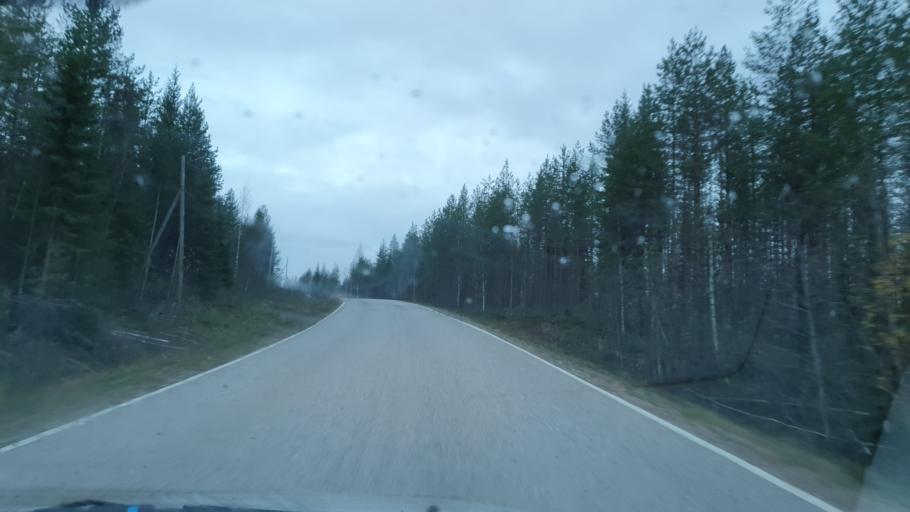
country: FI
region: Kainuu
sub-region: Kajaani
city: Ristijaervi
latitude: 64.4390
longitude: 28.3697
